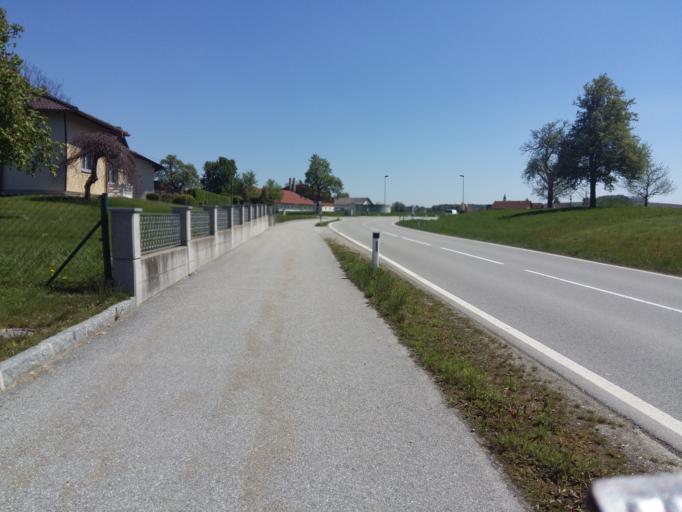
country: AT
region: Upper Austria
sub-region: Politischer Bezirk Scharding
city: Sankt Marienkirchen bei Schaerding
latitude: 48.3952
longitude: 13.4432
